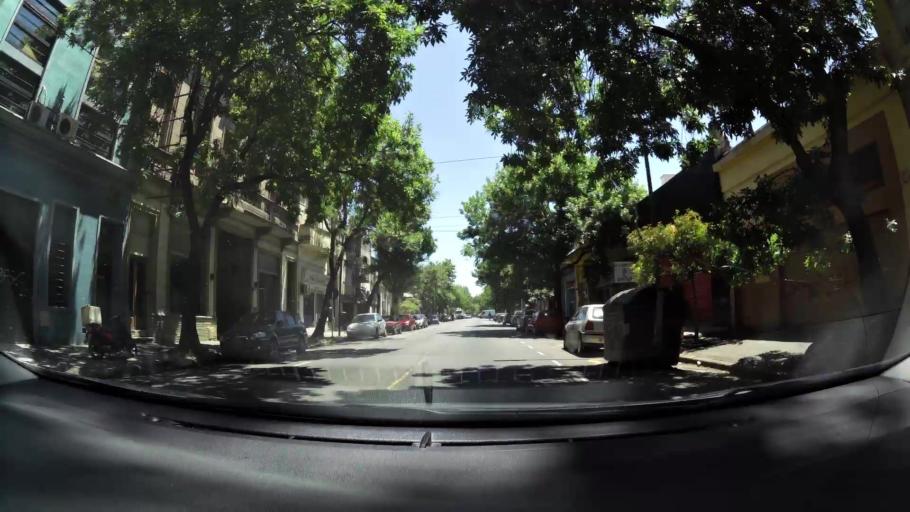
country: AR
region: Buenos Aires
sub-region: Partido de Avellaneda
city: Avellaneda
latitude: -34.6474
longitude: -58.3777
